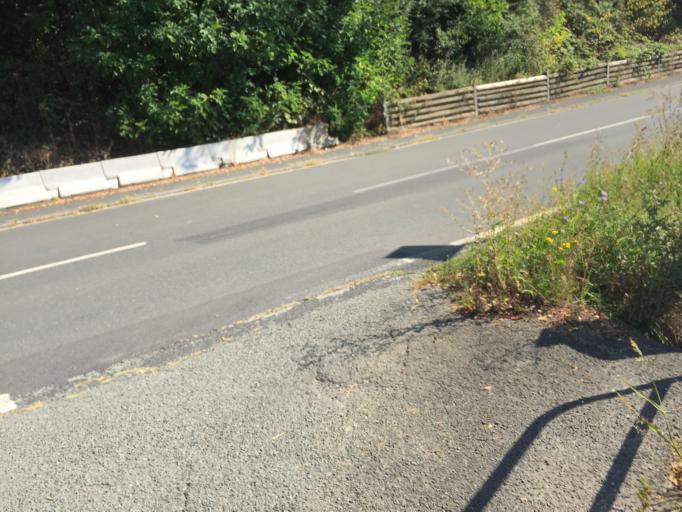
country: DE
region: Hesse
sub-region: Regierungsbezirk Giessen
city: Schoeffengrund
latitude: 50.4473
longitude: 8.5646
